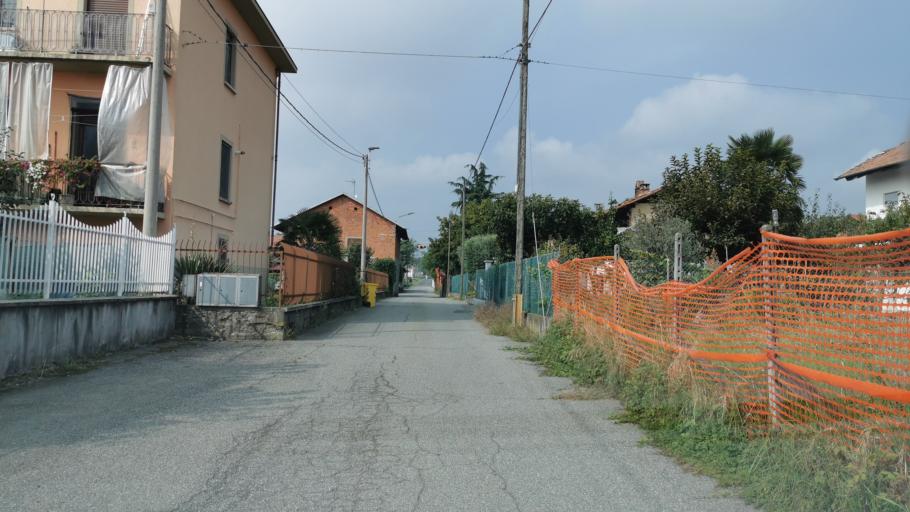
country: IT
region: Piedmont
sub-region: Provincia di Torino
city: Front
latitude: 45.2604
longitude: 7.6576
